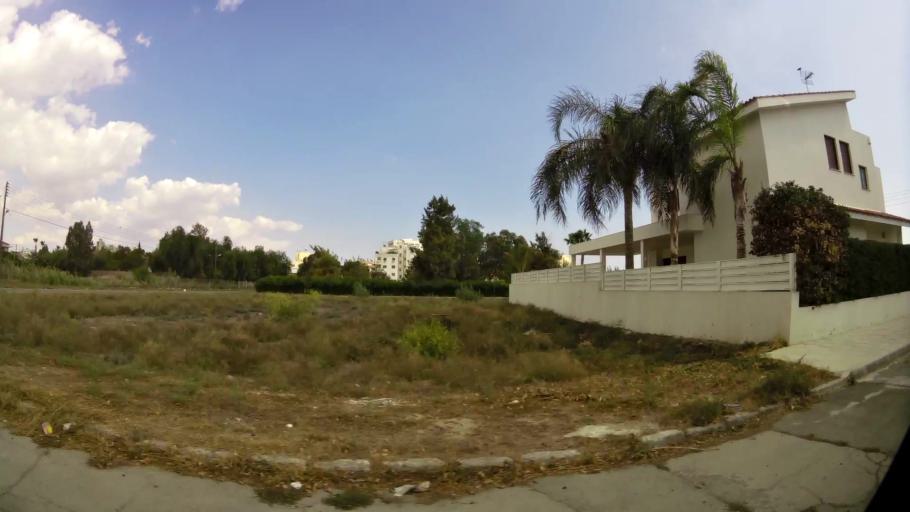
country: CY
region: Larnaka
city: Larnaca
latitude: 34.9132
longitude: 33.6242
